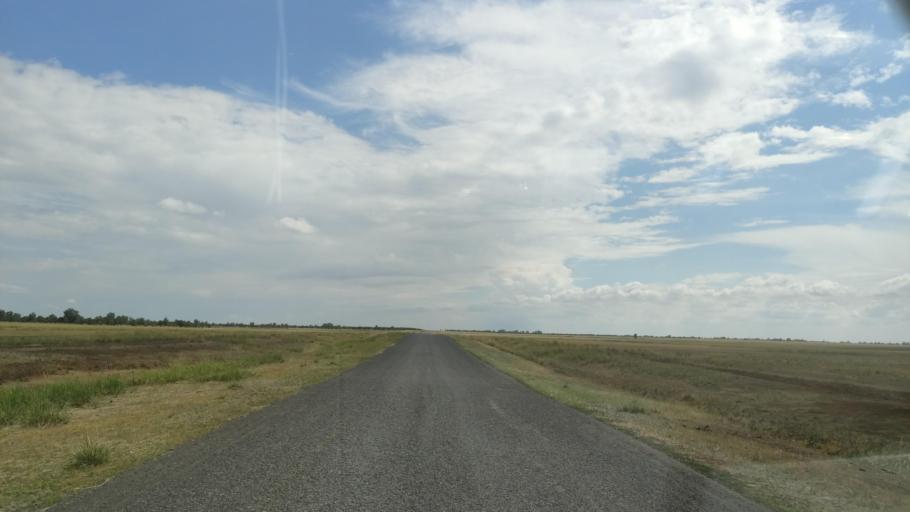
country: KZ
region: Pavlodar
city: Pavlodar
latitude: 52.6359
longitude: 76.9379
